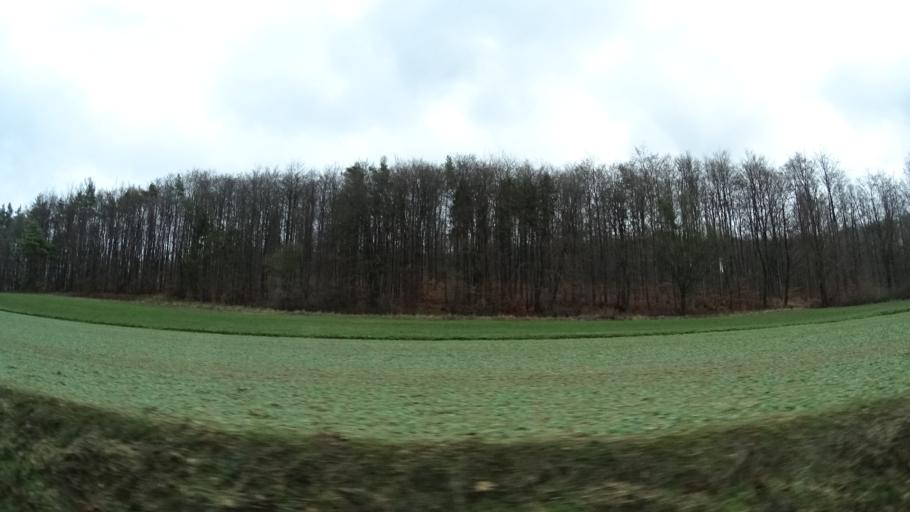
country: DE
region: Thuringia
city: Oberkatz
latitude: 50.5496
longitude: 10.2331
